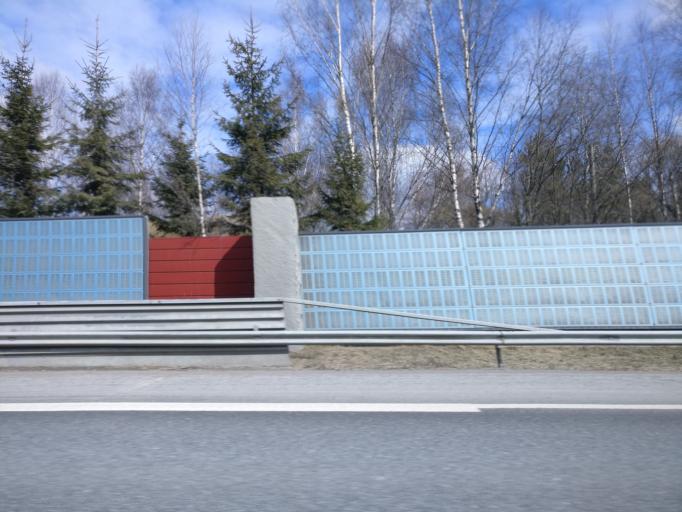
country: FI
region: Haeme
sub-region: Haemeenlinna
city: Haemeenlinna
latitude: 61.0020
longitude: 24.4493
